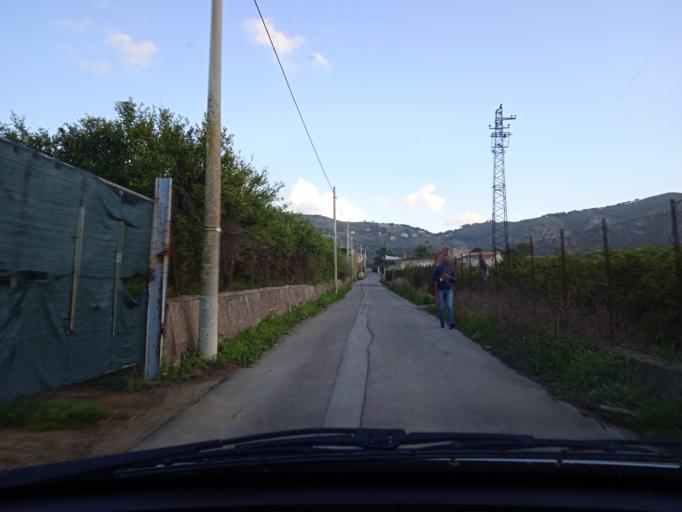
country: IT
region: Sicily
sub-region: Palermo
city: Villabate
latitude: 38.0812
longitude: 13.4261
